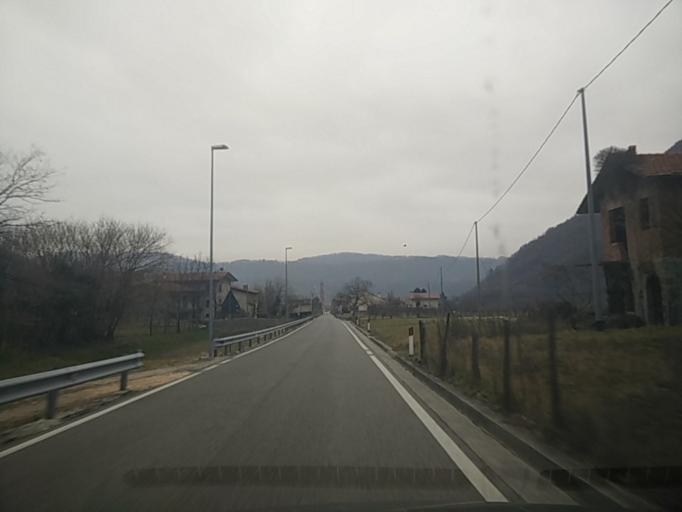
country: IT
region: Veneto
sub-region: Provincia di Treviso
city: Cison di Valmarino
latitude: 45.9836
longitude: 12.1732
